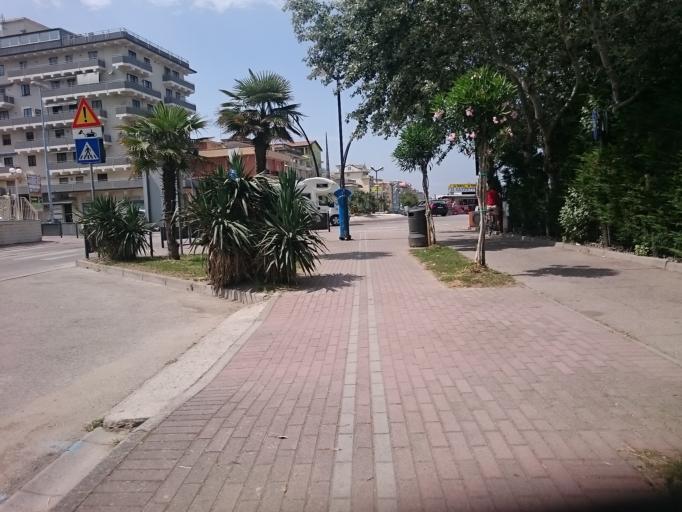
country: IT
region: Veneto
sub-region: Provincia di Venezia
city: Chioggia
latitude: 45.1985
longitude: 12.3006
